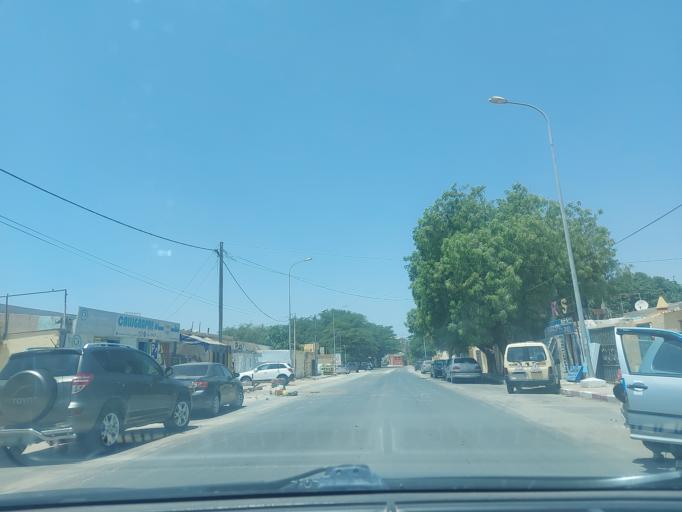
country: MR
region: Nouakchott
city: Nouakchott
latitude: 18.0891
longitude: -15.9812
